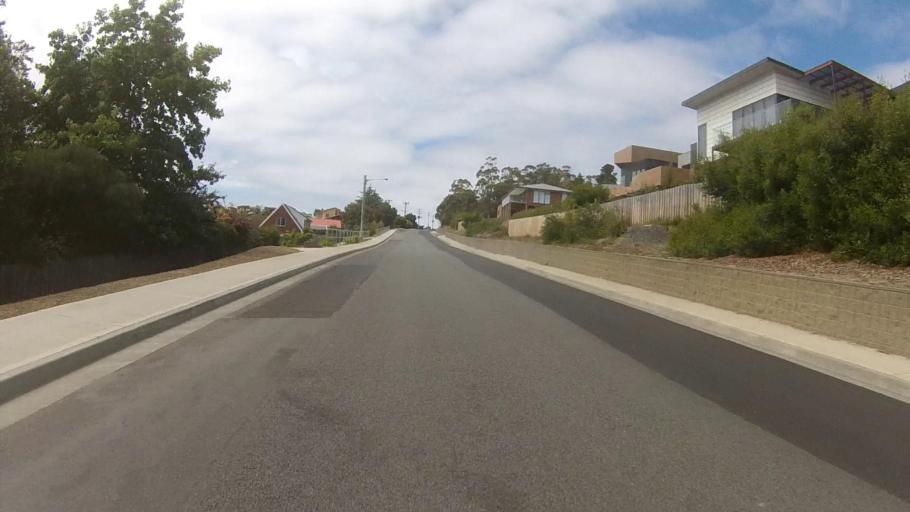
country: AU
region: Tasmania
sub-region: Kingborough
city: Blackmans Bay
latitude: -43.0111
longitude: 147.3197
